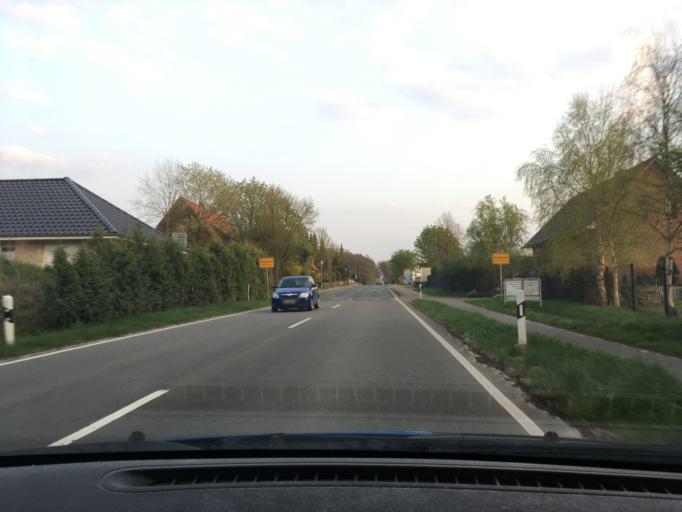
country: DE
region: Lower Saxony
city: Amelinghausen
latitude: 53.1375
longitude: 10.2134
